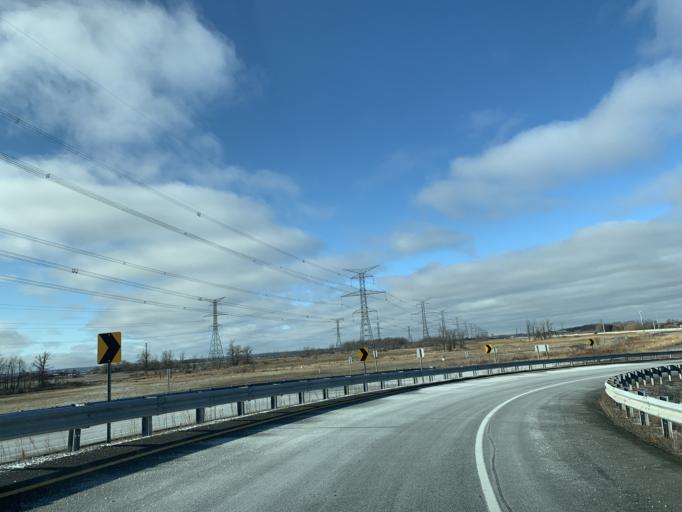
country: CA
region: Ontario
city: Mississauga
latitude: 43.5517
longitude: -79.7644
